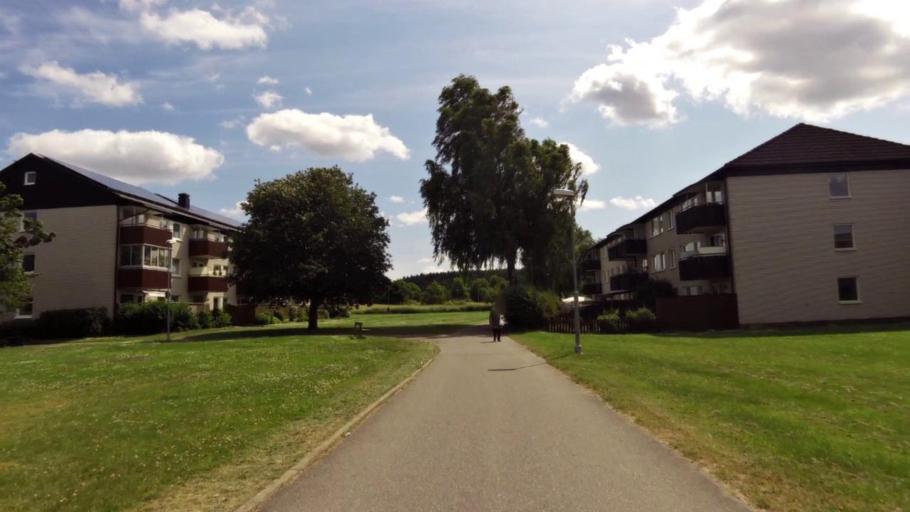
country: SE
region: OEstergoetland
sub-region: Linkopings Kommun
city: Linkoping
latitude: 58.4231
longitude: 15.5788
